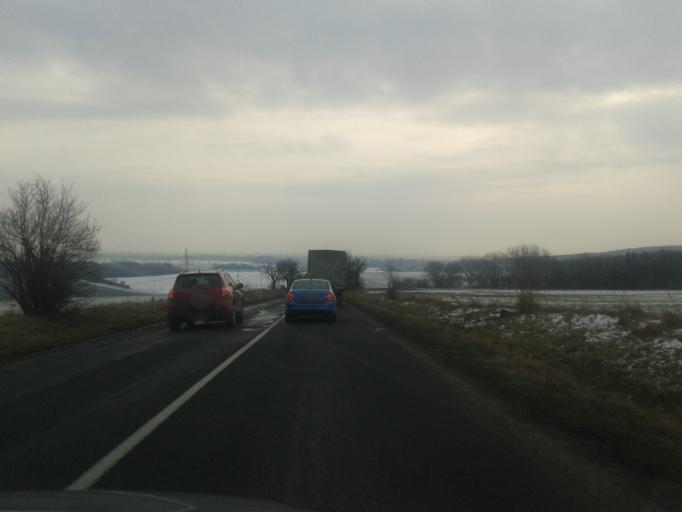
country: CZ
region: Olomoucky
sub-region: Okres Prostejov
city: Plumlov
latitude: 49.4824
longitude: 17.0195
